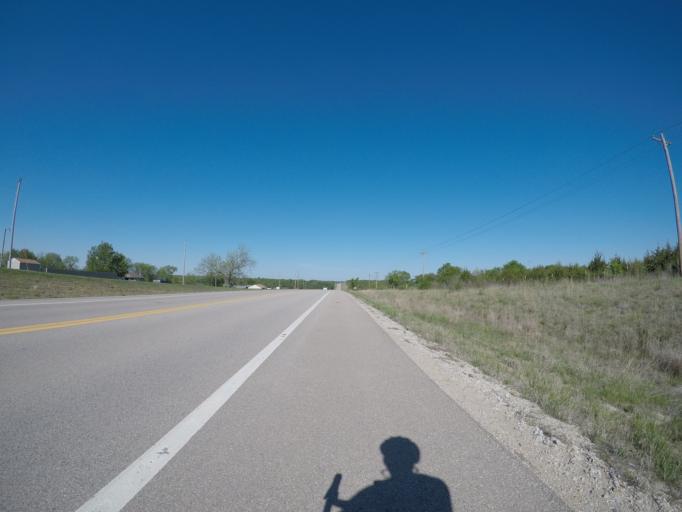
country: US
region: Kansas
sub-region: Douglas County
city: Lawrence
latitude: 38.9713
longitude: -95.4263
